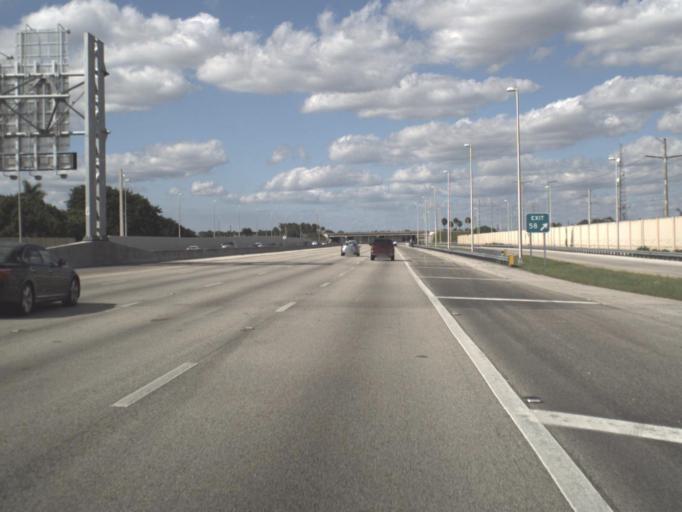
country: US
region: Florida
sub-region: Broward County
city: Lauderhill
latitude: 26.1309
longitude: -80.2179
